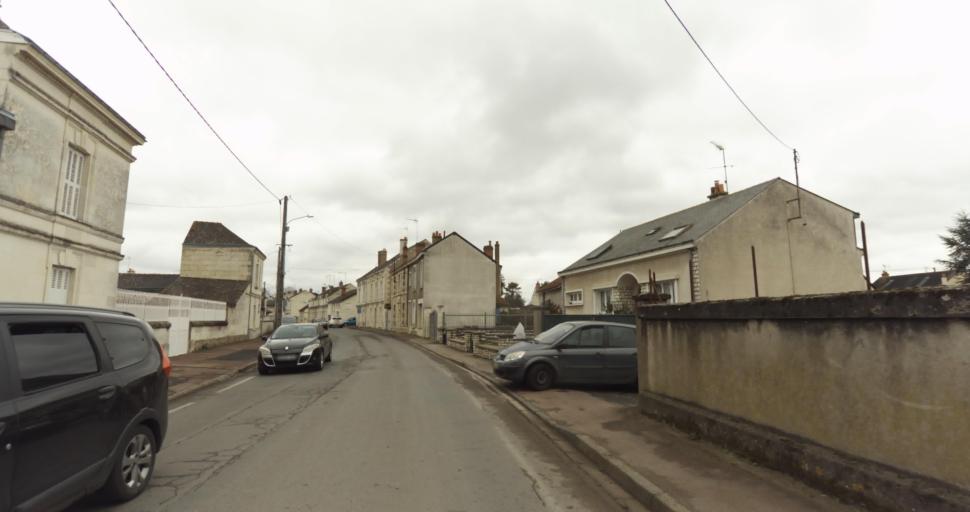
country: FR
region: Pays de la Loire
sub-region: Departement de Maine-et-Loire
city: Saumur
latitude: 47.2554
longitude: -0.0930
